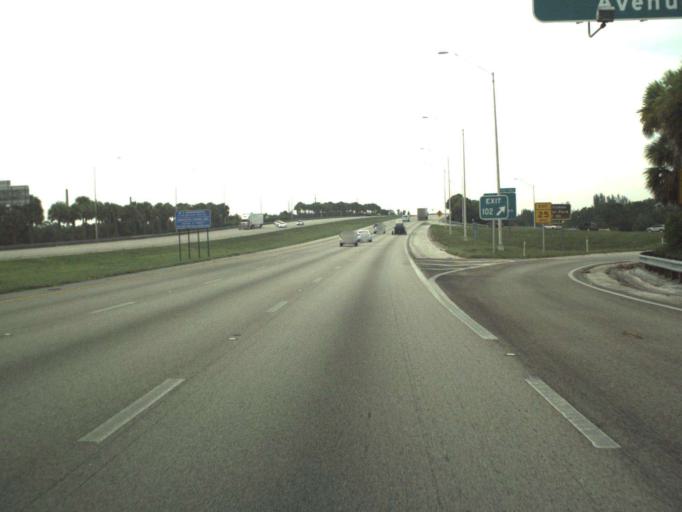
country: US
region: Florida
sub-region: Martin County
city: Palm City
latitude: 27.1237
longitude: -80.2771
